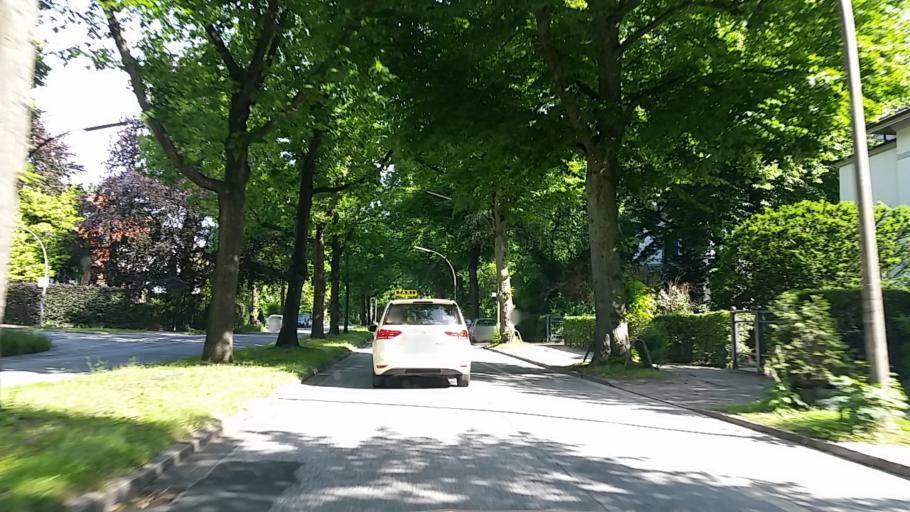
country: DE
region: Hamburg
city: Altona
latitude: 53.5582
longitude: 9.8882
